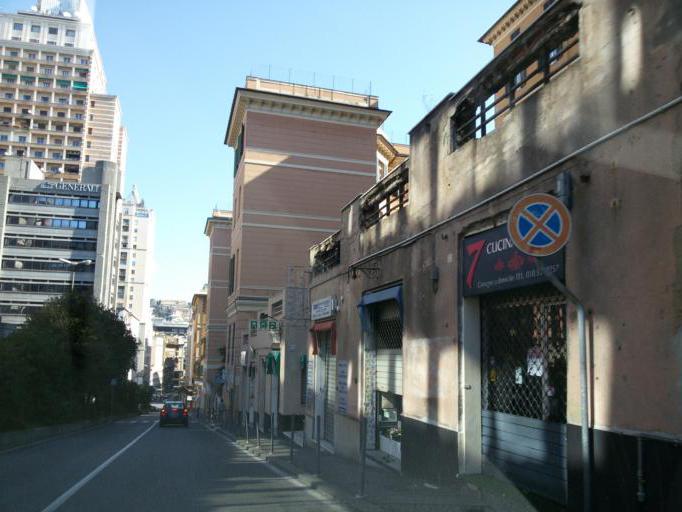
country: IT
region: Liguria
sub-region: Provincia di Genova
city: San Teodoro
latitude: 44.4033
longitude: 8.9354
